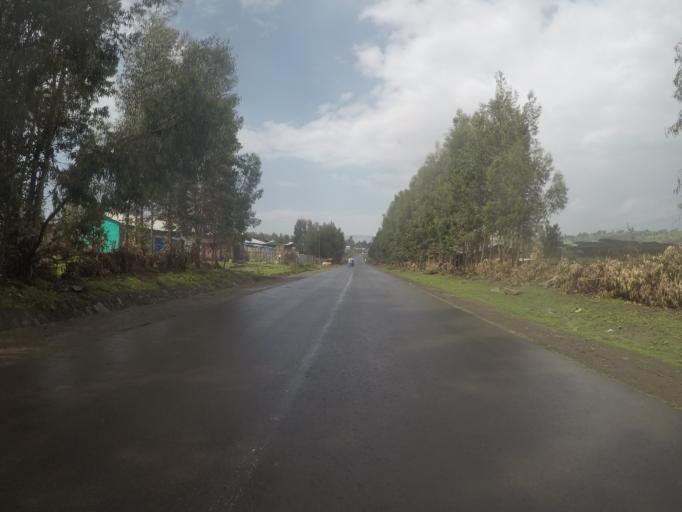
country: ET
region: Amhara
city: Debark'
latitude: 13.1214
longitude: 37.8828
